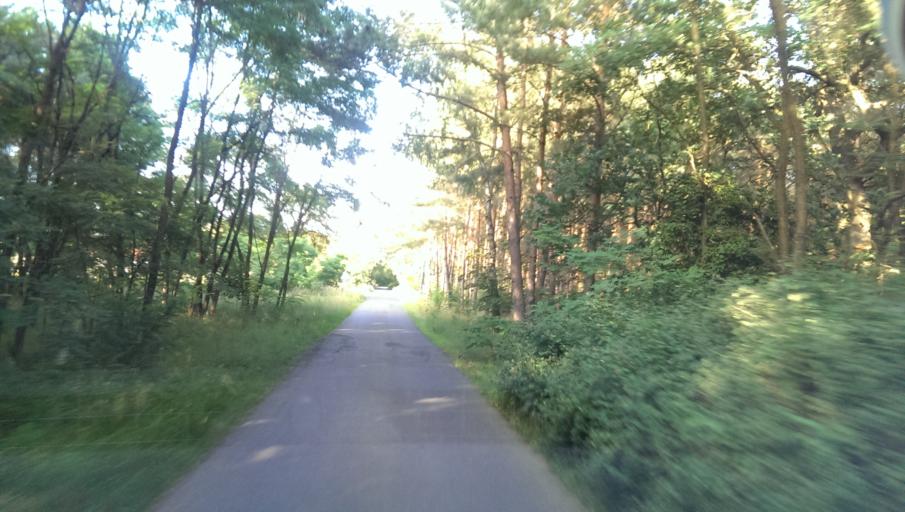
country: DE
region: Brandenburg
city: Treuenbrietzen
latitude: 52.0384
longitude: 12.8621
